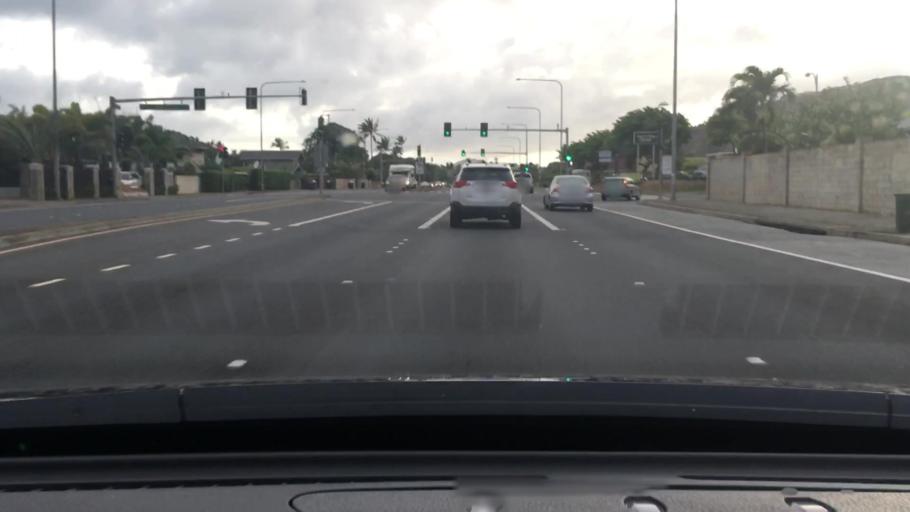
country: US
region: Hawaii
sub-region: Honolulu County
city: Waimanalo Beach
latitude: 21.2823
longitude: -157.7341
